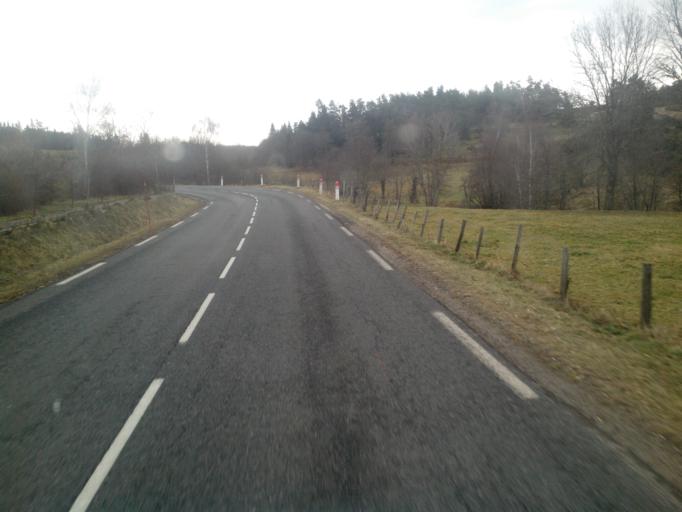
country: FR
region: Languedoc-Roussillon
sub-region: Departement de la Lozere
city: Mende
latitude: 44.6358
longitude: 3.4749
